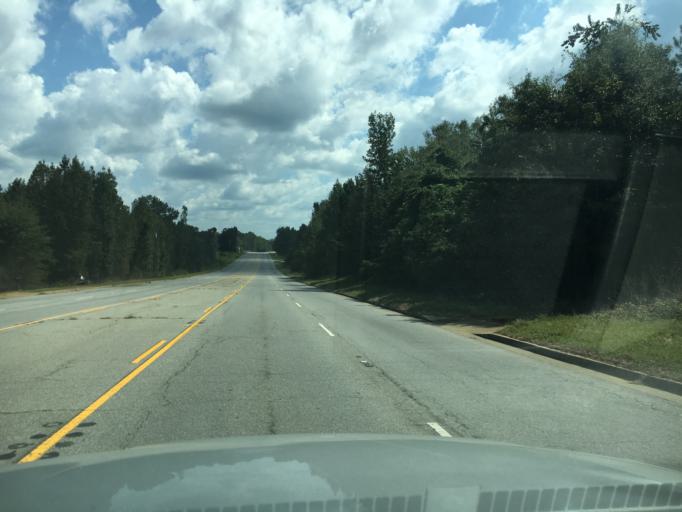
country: US
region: South Carolina
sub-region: Anderson County
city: Honea Path
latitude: 34.5097
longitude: -82.3038
